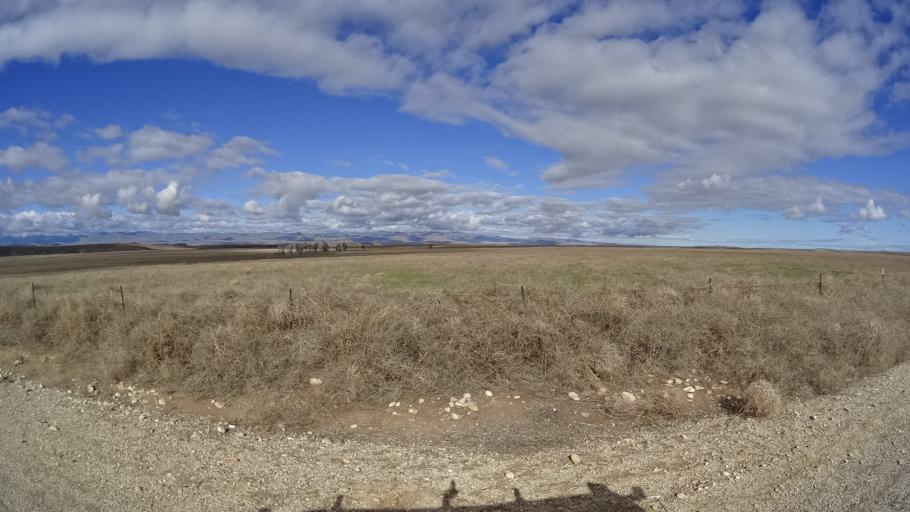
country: US
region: Idaho
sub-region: Owyhee County
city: Murphy
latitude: 43.3044
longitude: -116.4140
